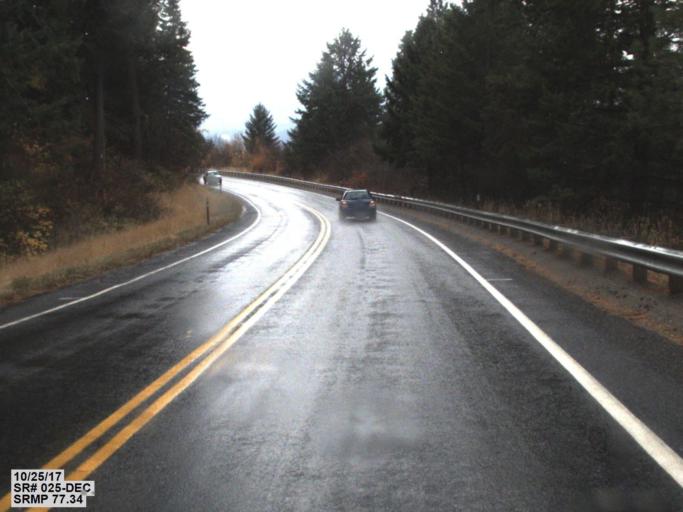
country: US
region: Washington
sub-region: Stevens County
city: Kettle Falls
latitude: 48.5702
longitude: -118.1085
